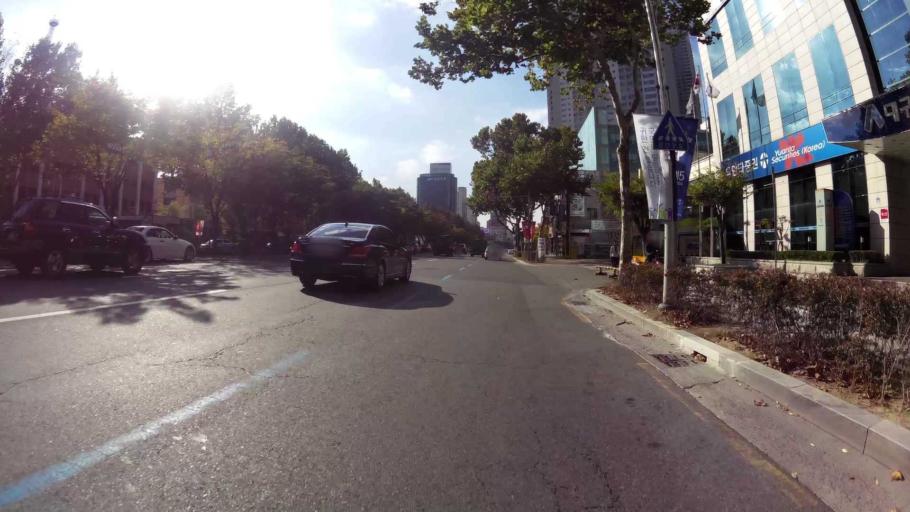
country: KR
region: Daegu
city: Daegu
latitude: 35.8589
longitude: 128.6319
